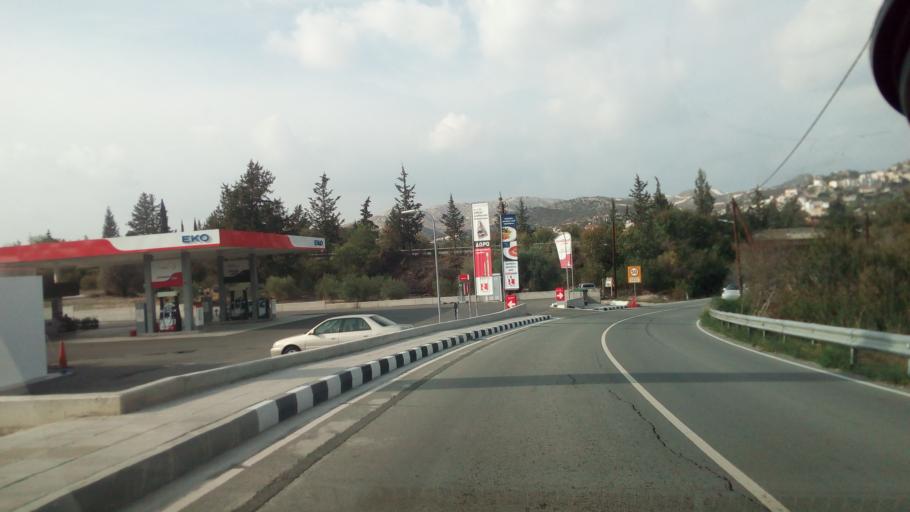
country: CY
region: Larnaka
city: Kofinou
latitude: 34.8152
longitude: 33.3613
